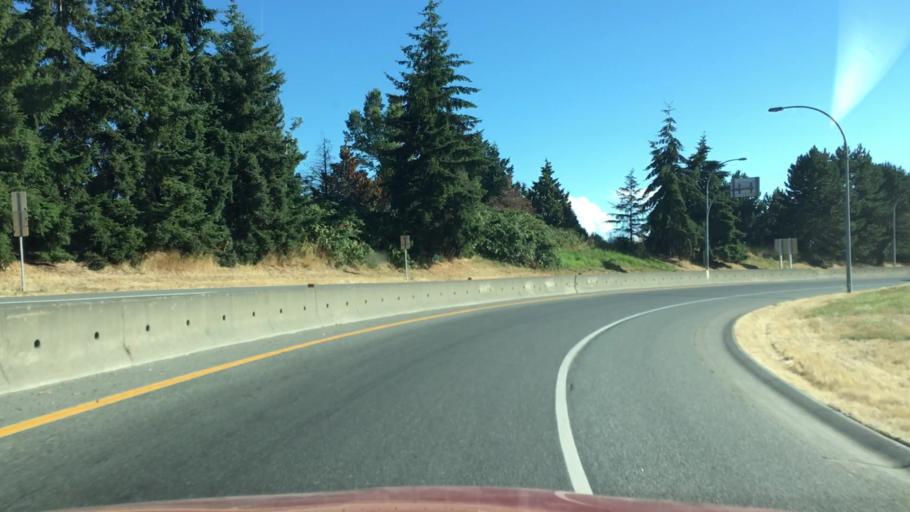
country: CA
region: British Columbia
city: Victoria
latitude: 48.4671
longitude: -123.3789
